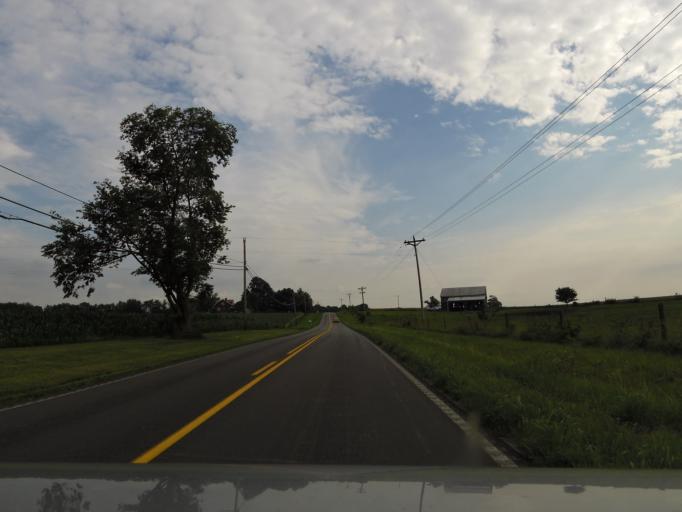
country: US
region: Kentucky
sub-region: Harrison County
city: Cynthiana
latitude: 38.4065
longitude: -84.2704
